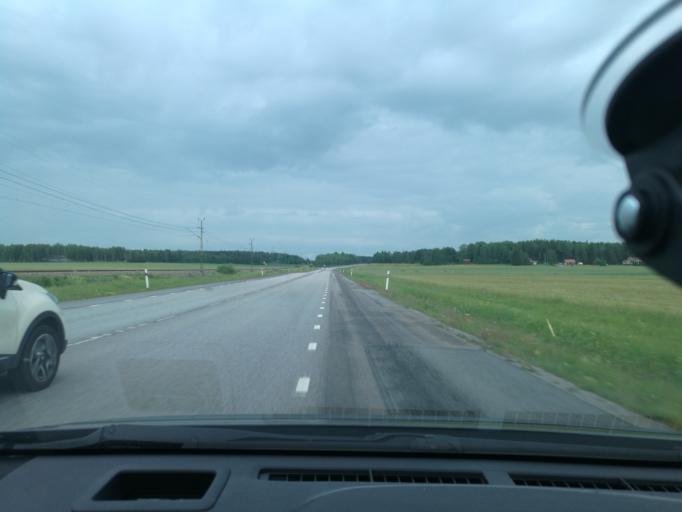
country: SE
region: Vaestmanland
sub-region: Sala Kommun
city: Sala
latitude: 59.9271
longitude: 16.6848
